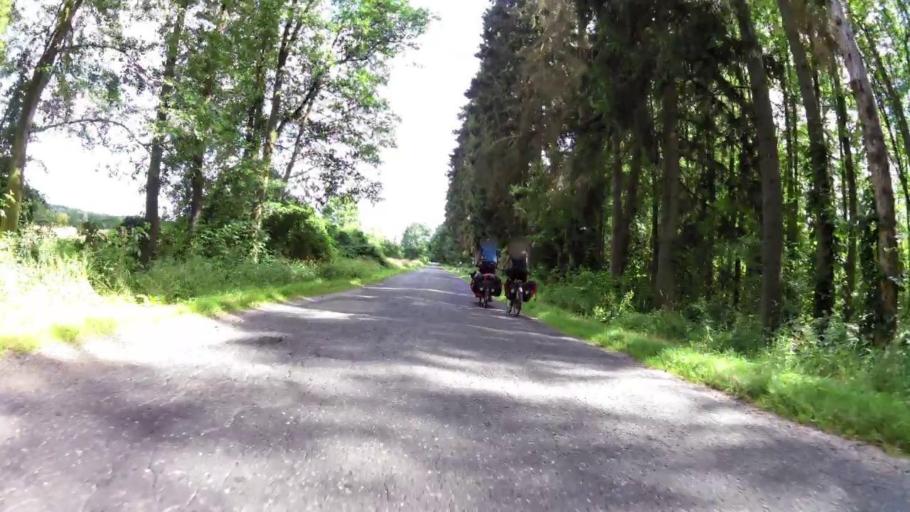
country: PL
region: West Pomeranian Voivodeship
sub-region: Powiat lobeski
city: Lobez
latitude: 53.6607
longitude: 15.5556
